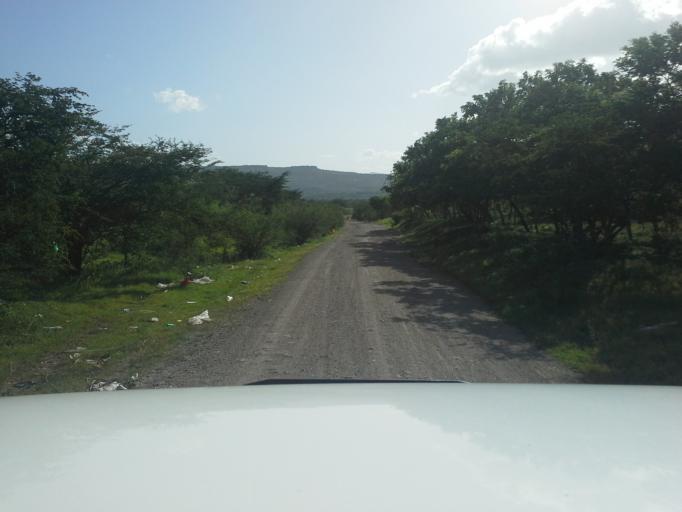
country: NI
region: Matagalpa
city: Ciudad Dario
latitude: 12.6588
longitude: -86.0765
